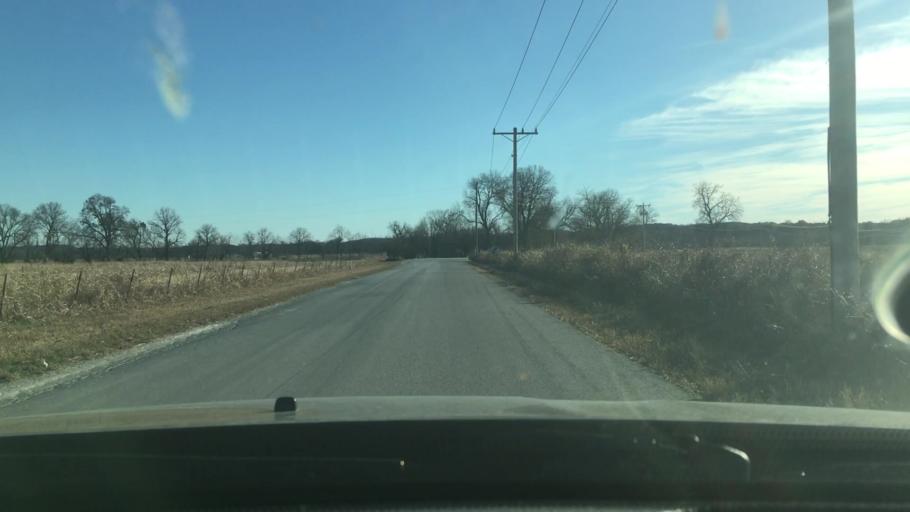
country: US
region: Oklahoma
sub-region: Murray County
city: Davis
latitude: 34.5008
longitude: -97.1559
